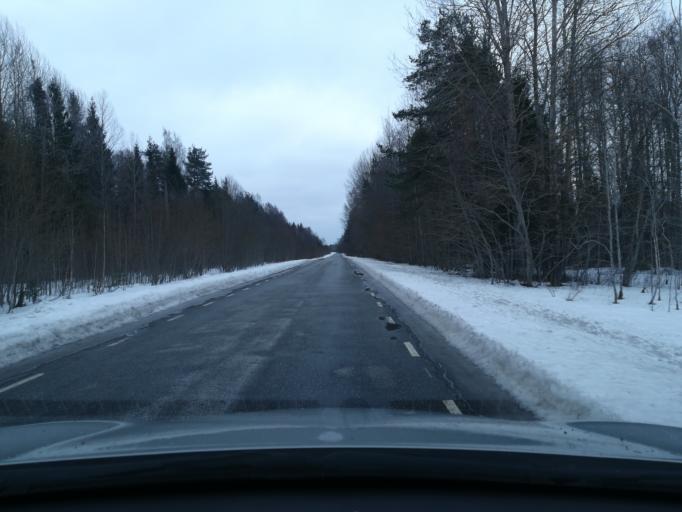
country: EE
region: Harju
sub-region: Nissi vald
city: Turba
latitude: 59.0647
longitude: 24.2535
